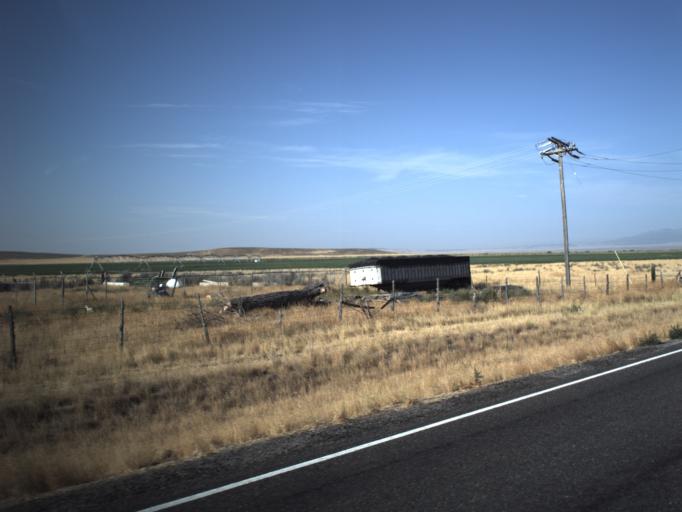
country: US
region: Idaho
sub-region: Oneida County
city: Malad City
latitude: 41.9663
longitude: -112.7742
